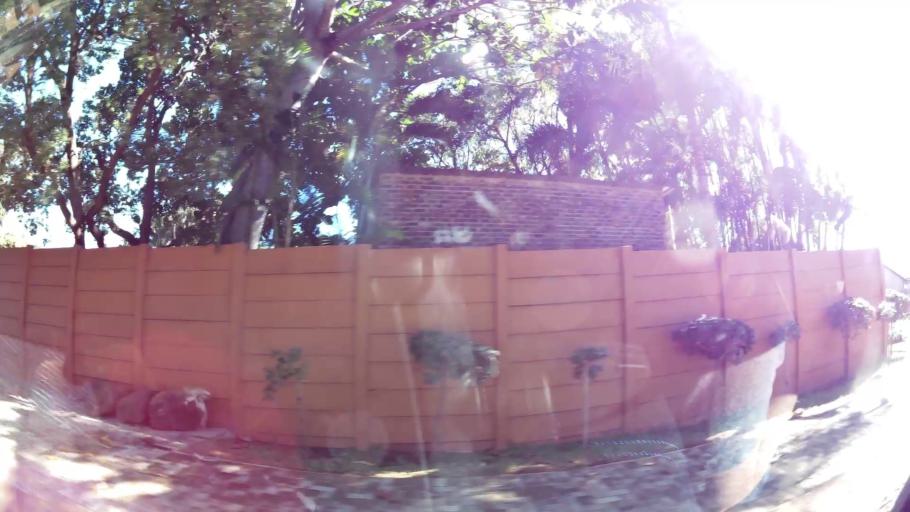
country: ZA
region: Limpopo
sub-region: Mopani District Municipality
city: Tzaneen
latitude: -23.8360
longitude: 30.1582
